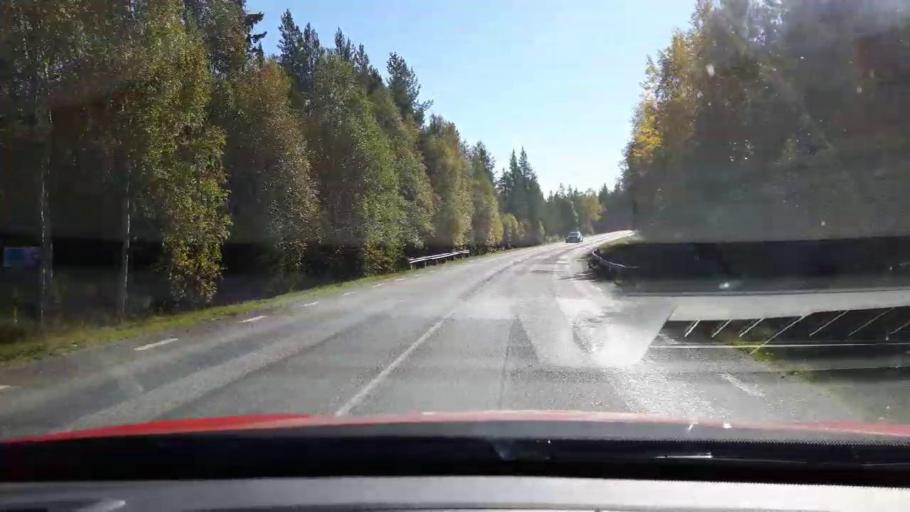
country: SE
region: Jaemtland
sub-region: Harjedalens Kommun
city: Sveg
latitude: 62.3522
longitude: 14.0278
